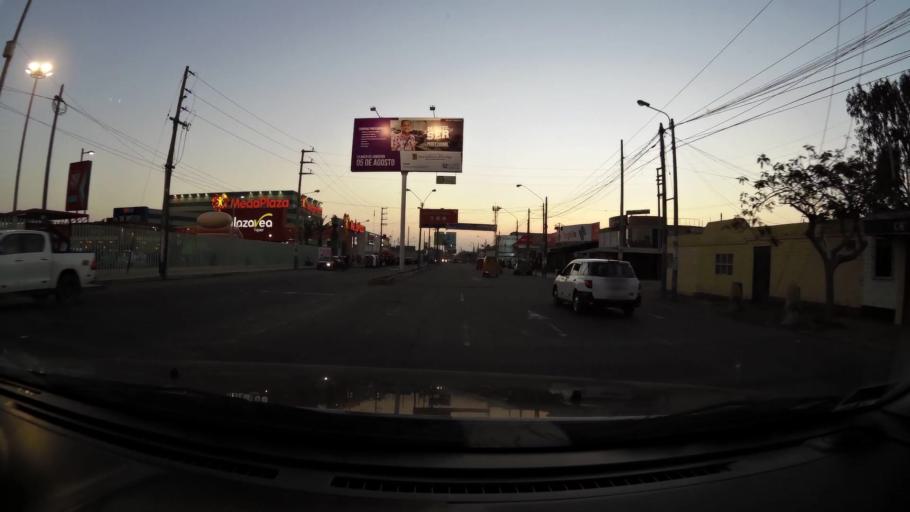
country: PE
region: Ica
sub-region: Provincia de Pisco
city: Pisco
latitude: -13.7109
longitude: -76.1945
